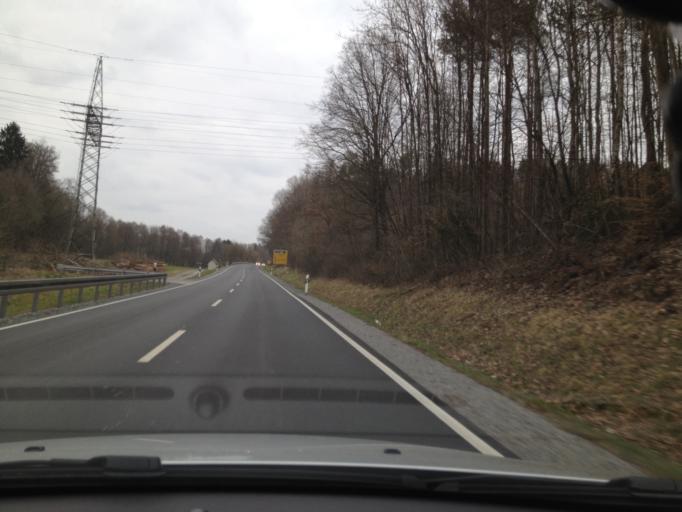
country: DE
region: Bavaria
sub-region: Regierungsbezirk Unterfranken
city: Kreuzwertheim
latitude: 49.7949
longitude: 9.5475
